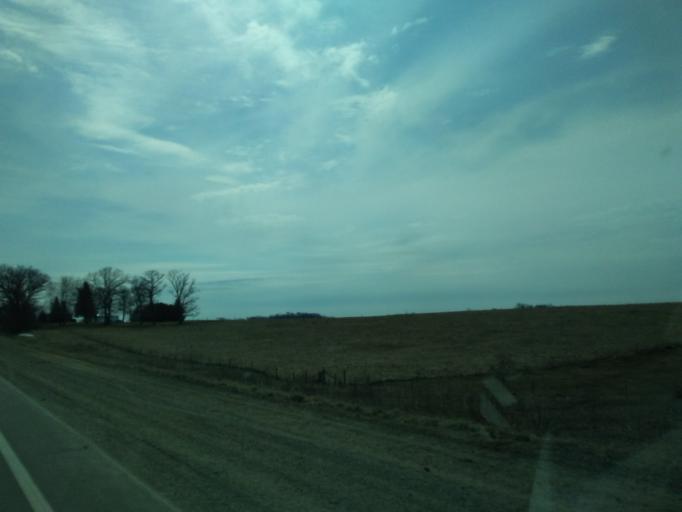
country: US
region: Iowa
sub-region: Winneshiek County
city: Decorah
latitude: 43.4247
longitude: -91.8593
